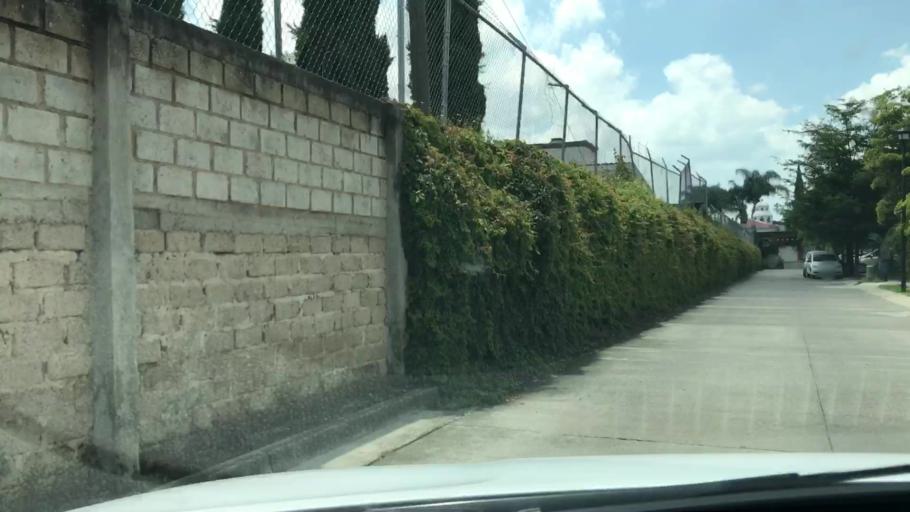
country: MX
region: Jalisco
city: Nuevo Mexico
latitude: 20.7520
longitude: -103.4269
